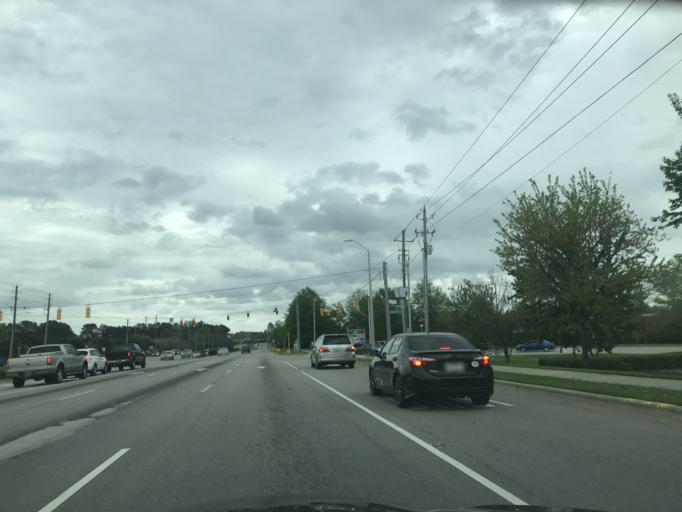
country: US
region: North Carolina
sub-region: Wake County
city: Knightdale
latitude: 35.7965
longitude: -78.5066
